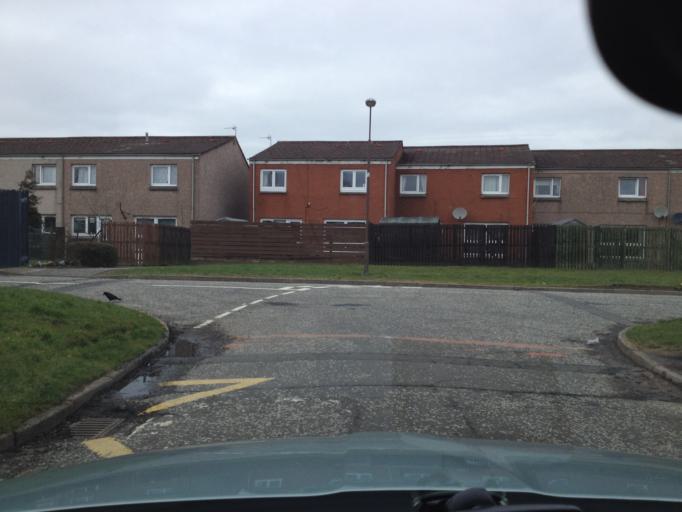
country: GB
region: Scotland
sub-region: West Lothian
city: Mid Calder
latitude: 55.8827
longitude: -3.4995
